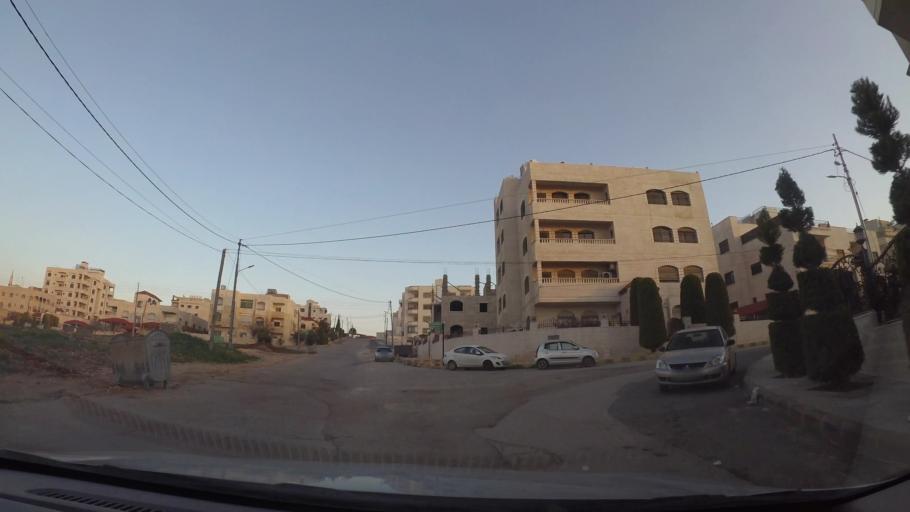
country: JO
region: Amman
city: Al Quwaysimah
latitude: 31.8978
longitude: 35.9256
